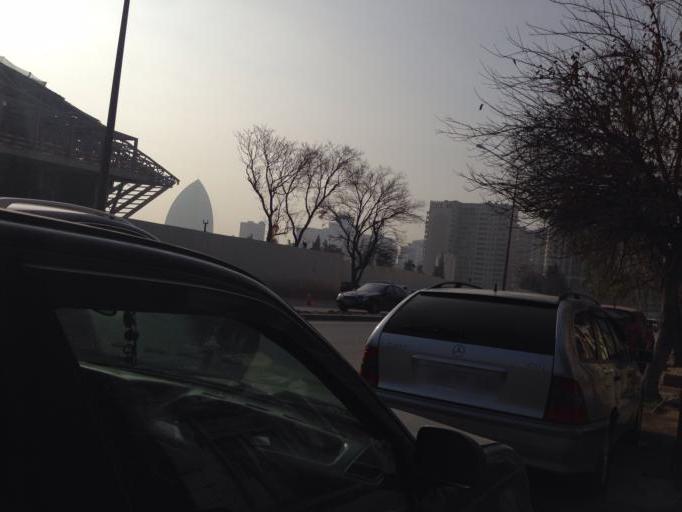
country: AZ
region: Baki
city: Baku
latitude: 40.3981
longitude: 49.8649
